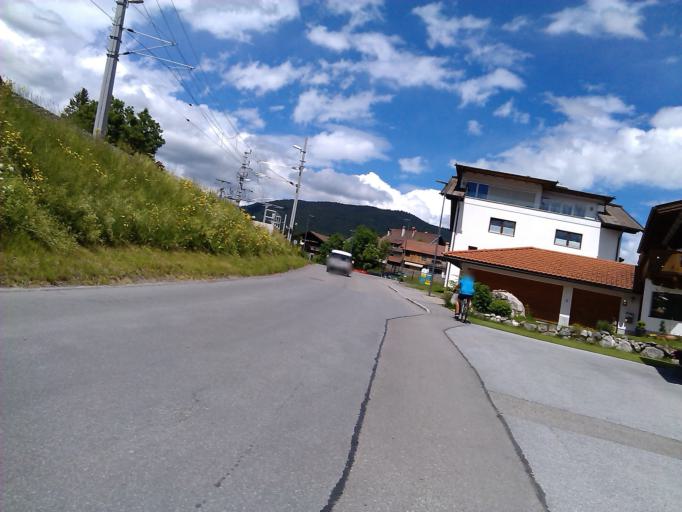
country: AT
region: Tyrol
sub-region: Politischer Bezirk Reutte
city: Ehrwald
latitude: 47.4081
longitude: 10.9130
